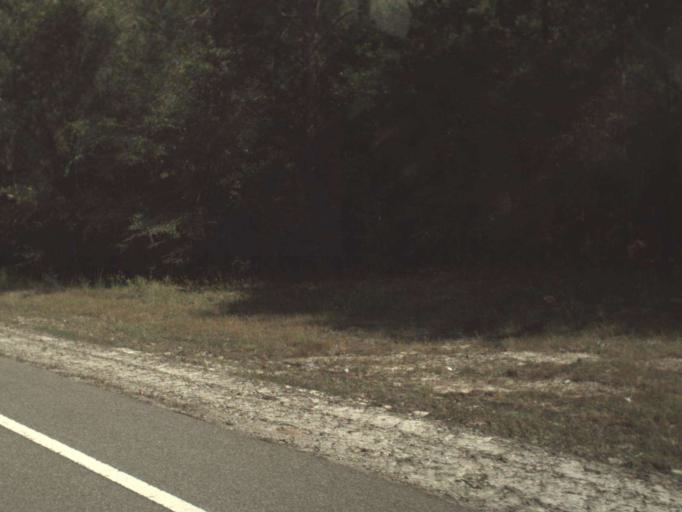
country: US
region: Florida
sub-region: Walton County
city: DeFuniak Springs
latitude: 30.8859
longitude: -86.1260
